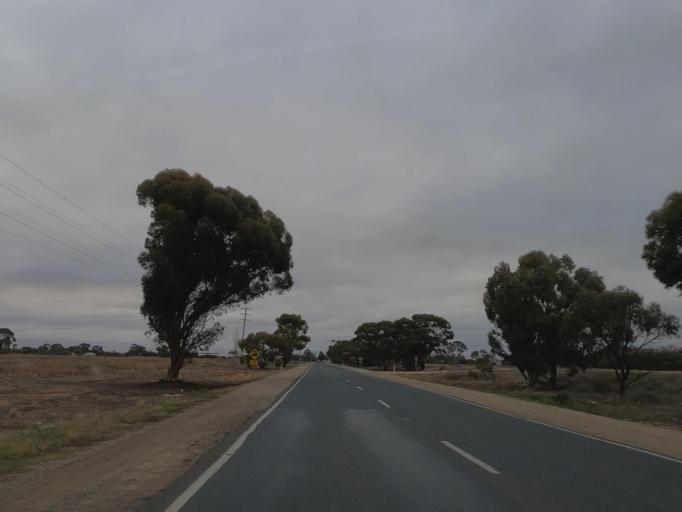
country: AU
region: Victoria
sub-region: Swan Hill
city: Swan Hill
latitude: -35.3936
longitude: 143.5717
